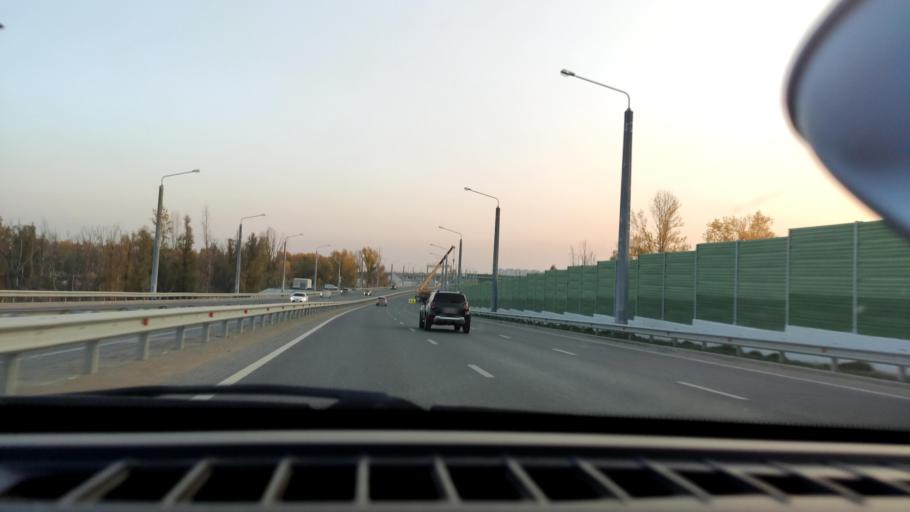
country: RU
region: Samara
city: Samara
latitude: 53.1721
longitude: 50.0865
